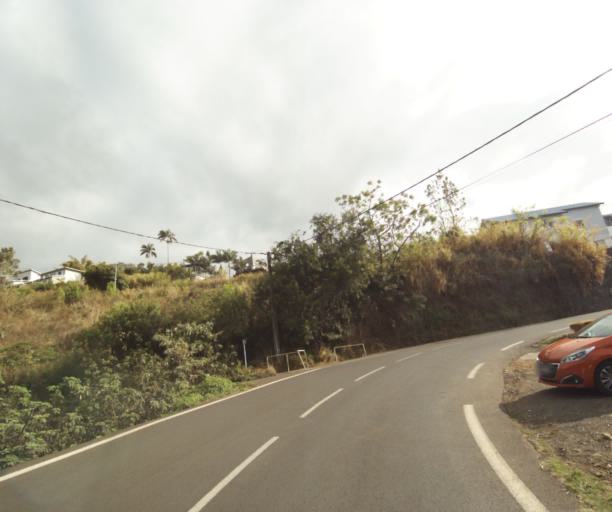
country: RE
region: Reunion
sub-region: Reunion
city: Saint-Paul
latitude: -21.0302
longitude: 55.3116
